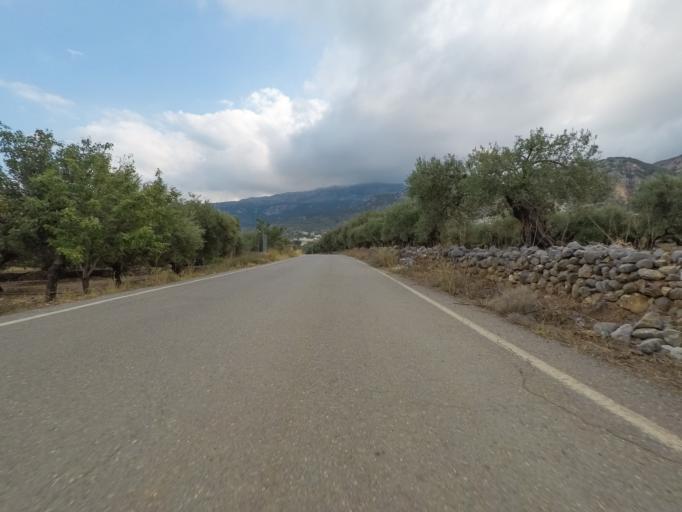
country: GR
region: Crete
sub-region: Nomos Lasithiou
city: Kritsa
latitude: 35.1627
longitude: 25.6519
